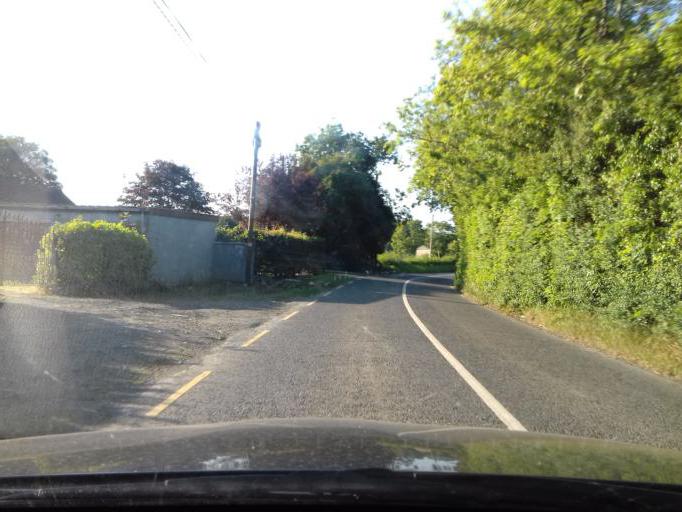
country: IE
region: Leinster
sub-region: An Mhi
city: Ashbourne
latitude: 53.5488
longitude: -6.3751
